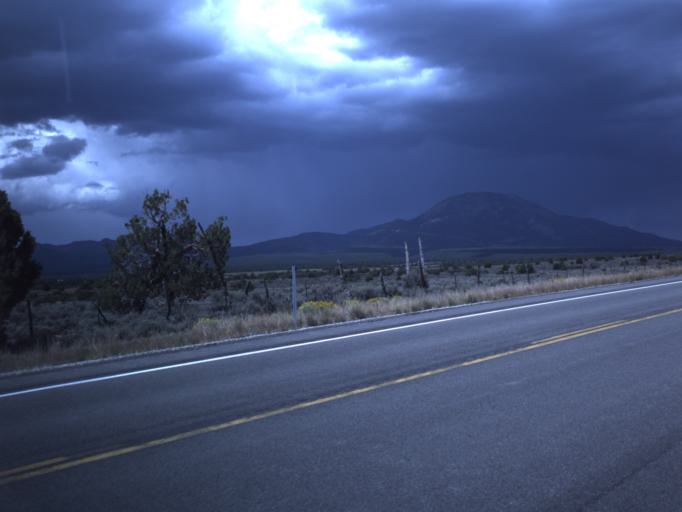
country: US
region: Utah
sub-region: San Juan County
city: Blanding
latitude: 37.7154
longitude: -109.4207
